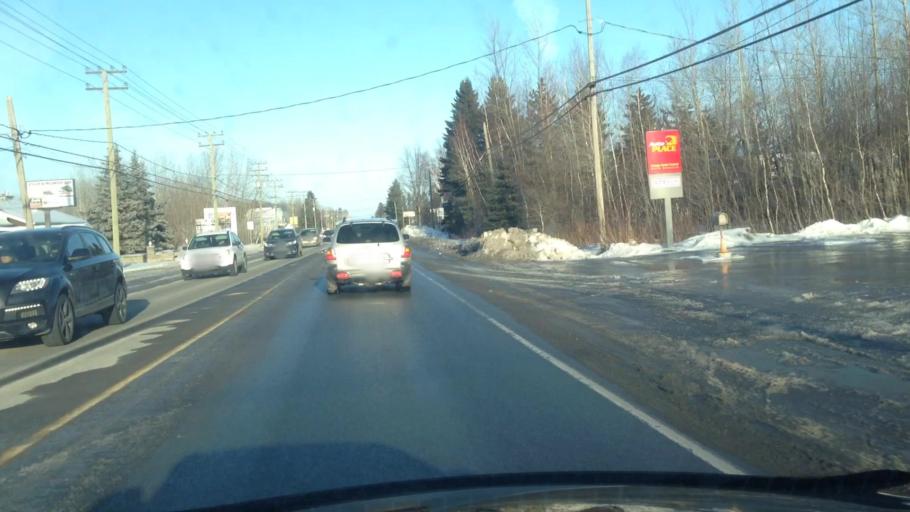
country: CA
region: Quebec
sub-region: Laurentides
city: Saint-Jerome
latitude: 45.7726
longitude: -73.9702
